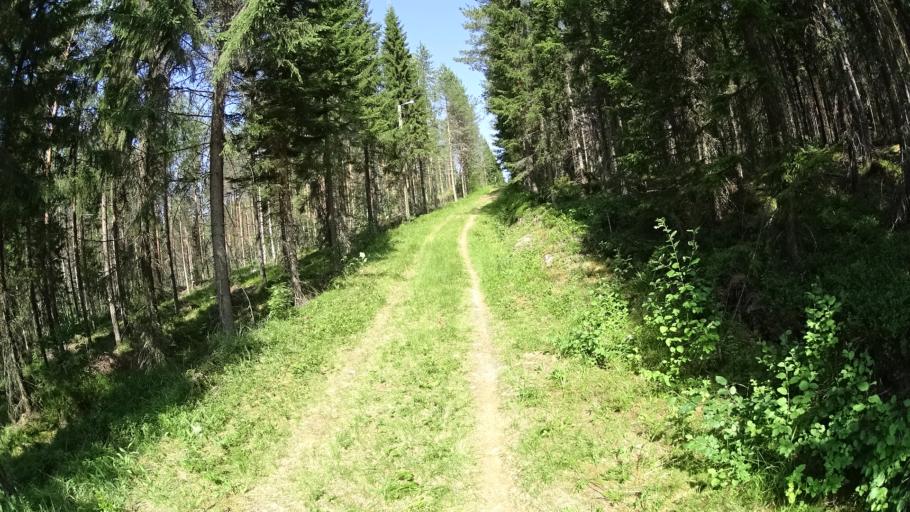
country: FI
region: North Karelia
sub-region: Pielisen Karjala
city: Lieksa
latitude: 63.1251
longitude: 29.8002
